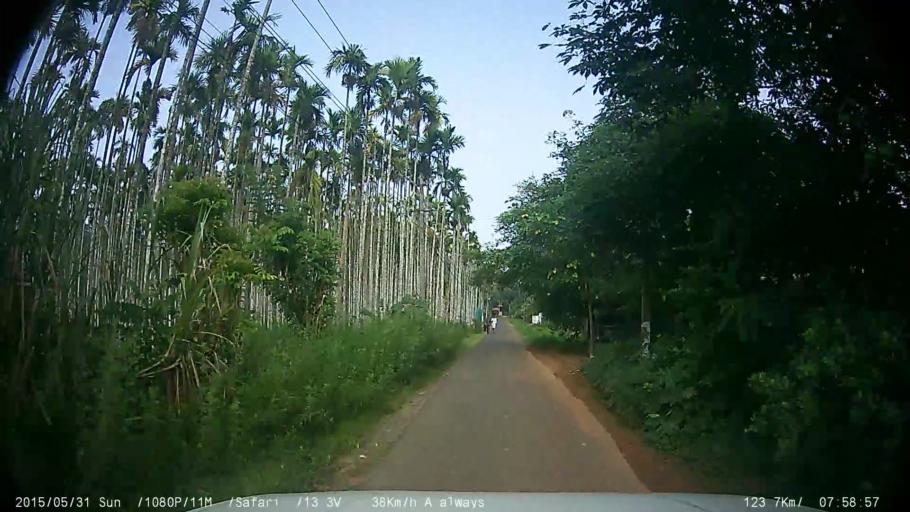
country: IN
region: Kerala
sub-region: Wayanad
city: Kalpetta
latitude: 11.6351
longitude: 76.0597
